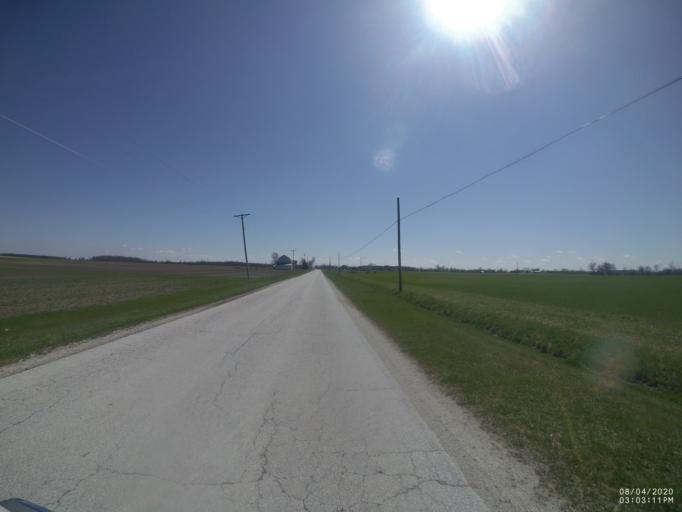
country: US
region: Ohio
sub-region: Sandusky County
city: Stony Prairie
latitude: 41.3291
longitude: -83.2398
